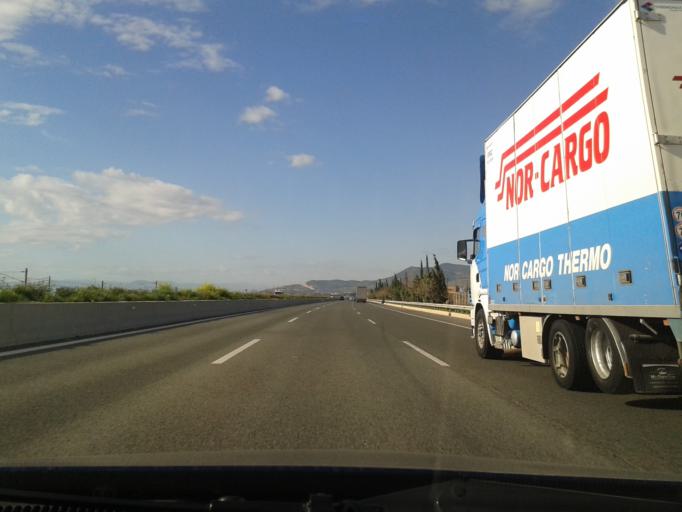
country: GR
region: Attica
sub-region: Nomarchia Dytikis Attikis
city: Nea Peramos
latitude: 38.0096
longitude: 23.4050
